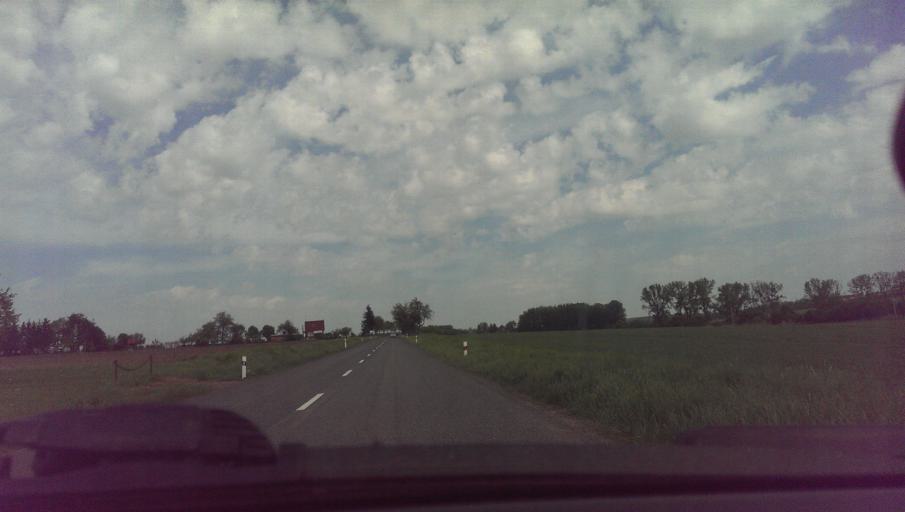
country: CZ
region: Zlin
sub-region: Okres Zlin
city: Otrokovice
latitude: 49.2235
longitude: 17.5364
